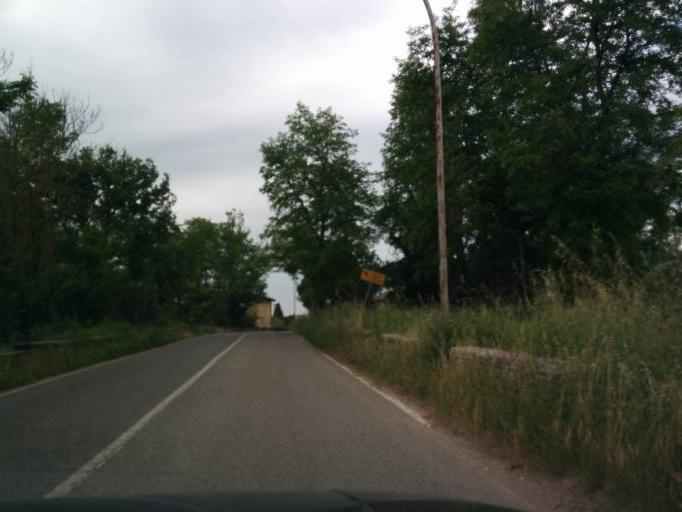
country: IT
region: Tuscany
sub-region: Province of Florence
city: San Casciano in Val di Pesa
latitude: 43.6332
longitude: 11.1799
